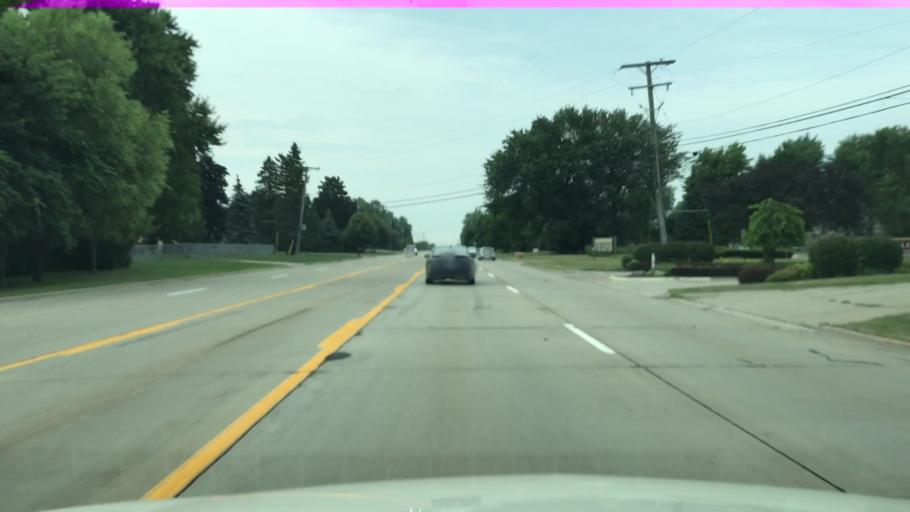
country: US
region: Michigan
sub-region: Macomb County
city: Fraser
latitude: 42.5737
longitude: -82.9711
